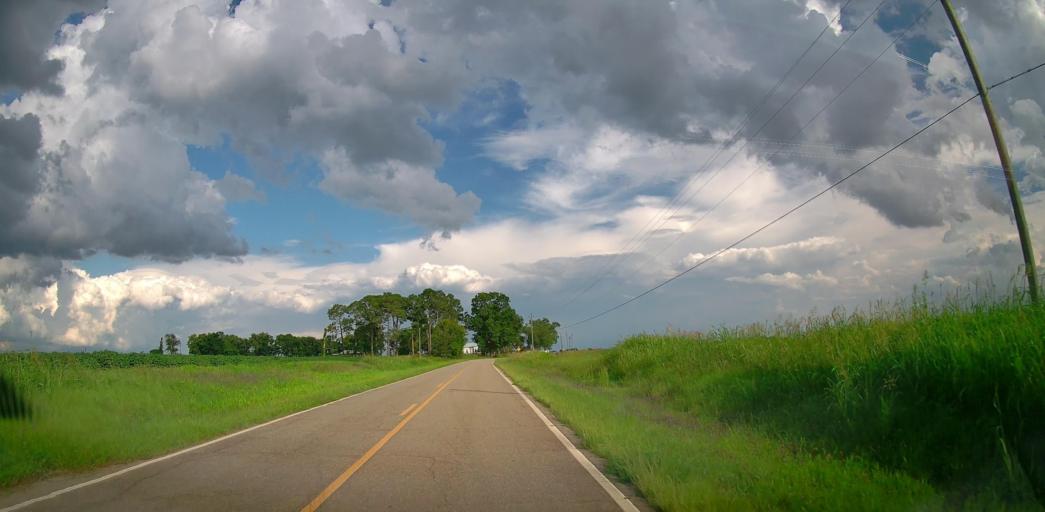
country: US
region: Georgia
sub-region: Bleckley County
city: Cochran
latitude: 32.4020
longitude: -83.3769
